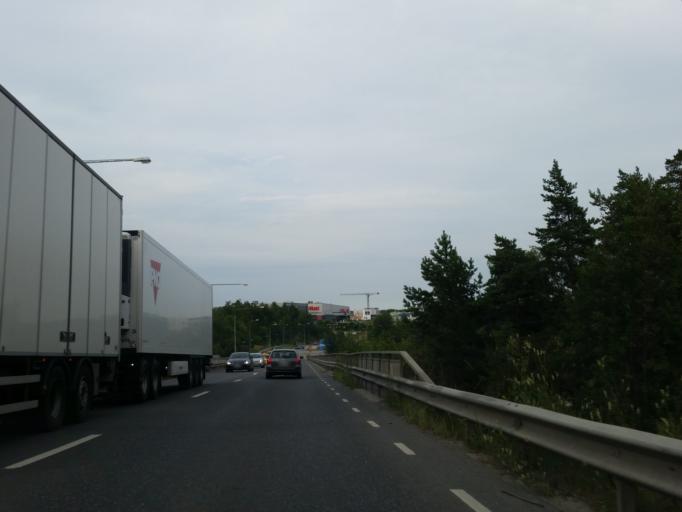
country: SE
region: Stockholm
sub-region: Jarfalla Kommun
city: Jakobsberg
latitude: 59.4098
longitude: 17.8484
